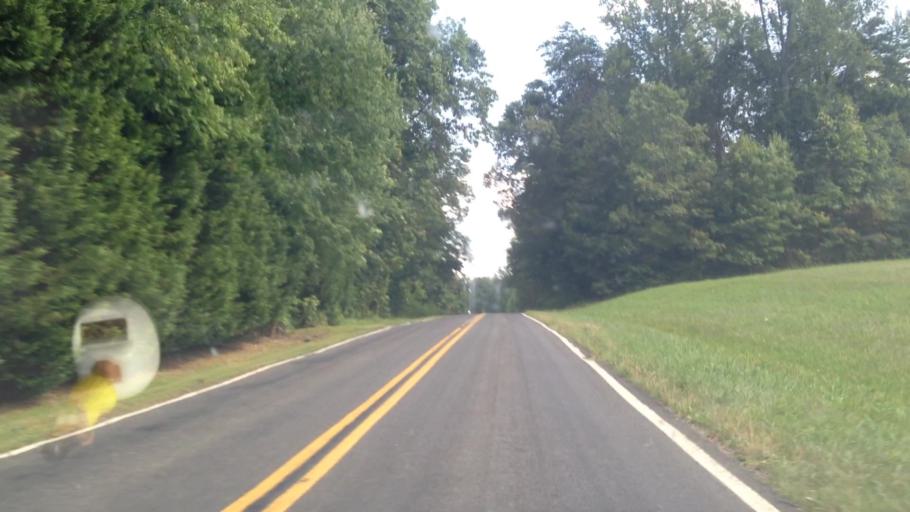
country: US
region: North Carolina
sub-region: Forsyth County
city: Walkertown
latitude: 36.2097
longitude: -80.1097
